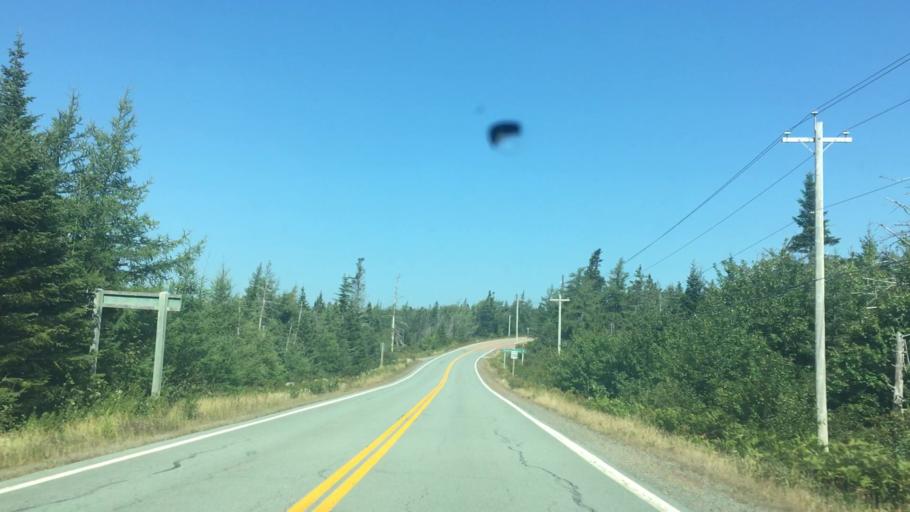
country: CA
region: Nova Scotia
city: Antigonish
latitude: 45.0225
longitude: -62.0312
